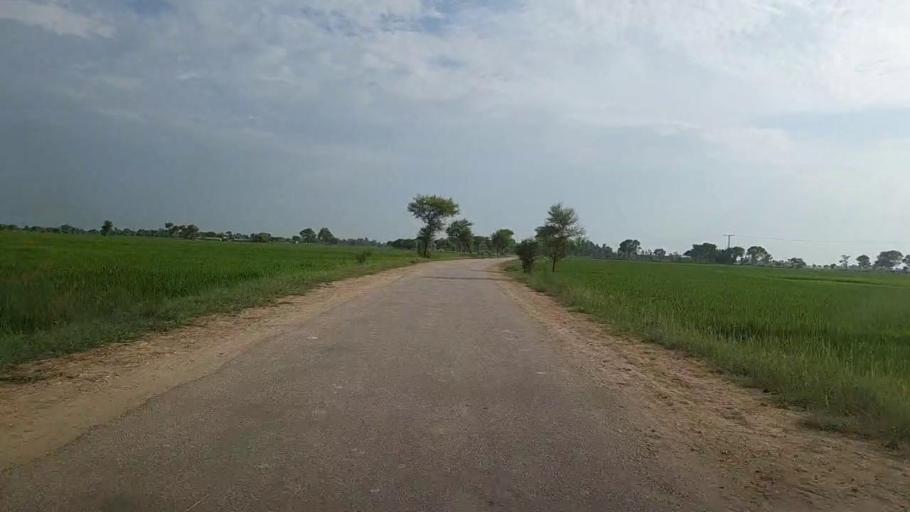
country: PK
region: Sindh
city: Thul
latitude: 28.2610
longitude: 68.8589
